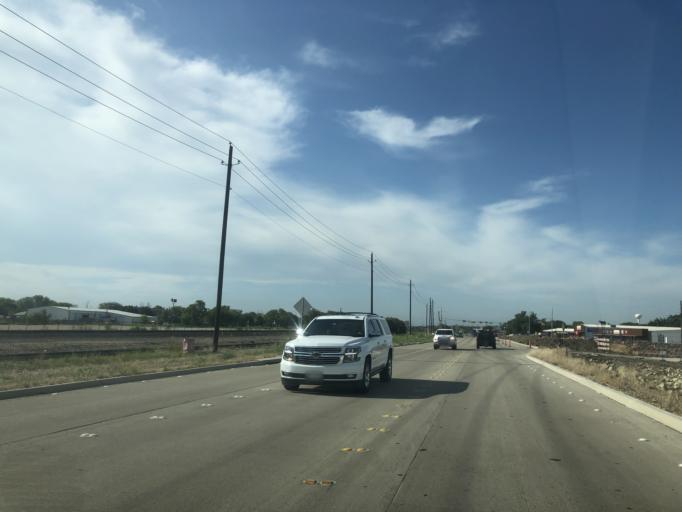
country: US
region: Texas
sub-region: Denton County
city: Justin
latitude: 33.0872
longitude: -97.2954
